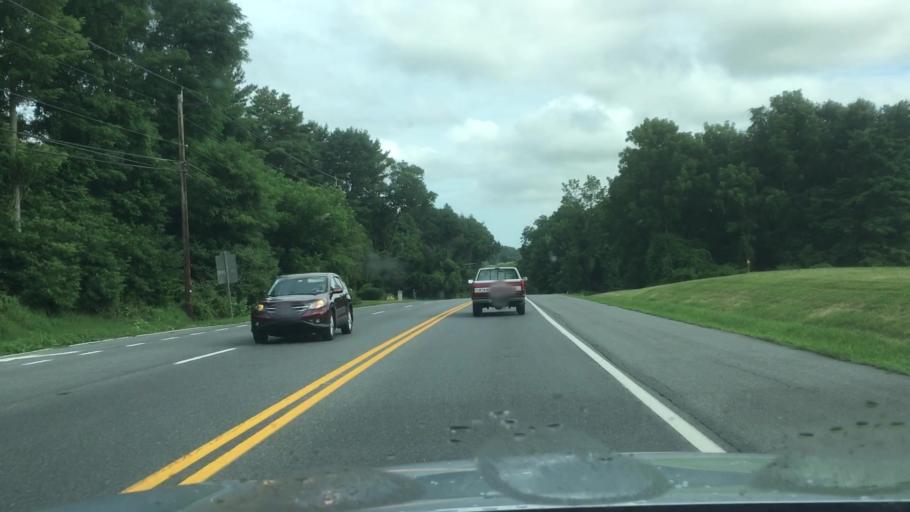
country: US
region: Delaware
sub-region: New Castle County
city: North Star
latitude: 39.7811
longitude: -75.7211
